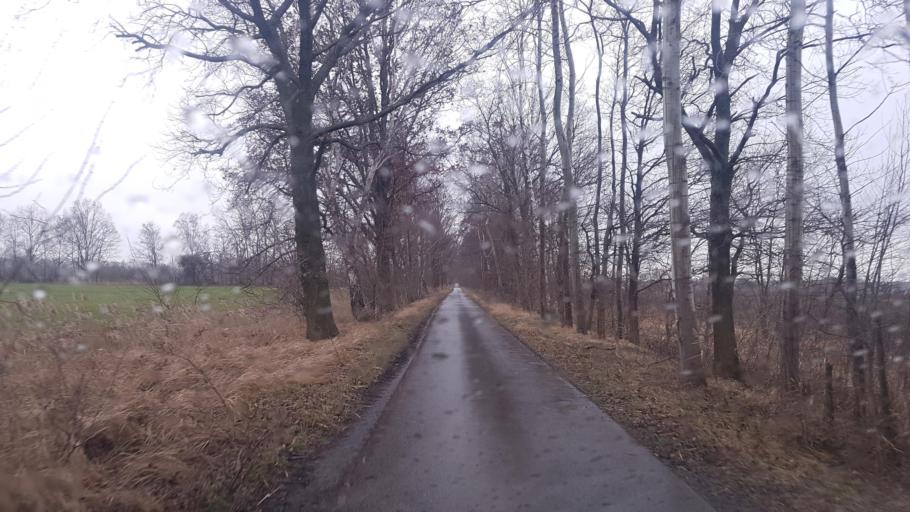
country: DE
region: Brandenburg
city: Grossthiemig
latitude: 51.4155
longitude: 13.6496
